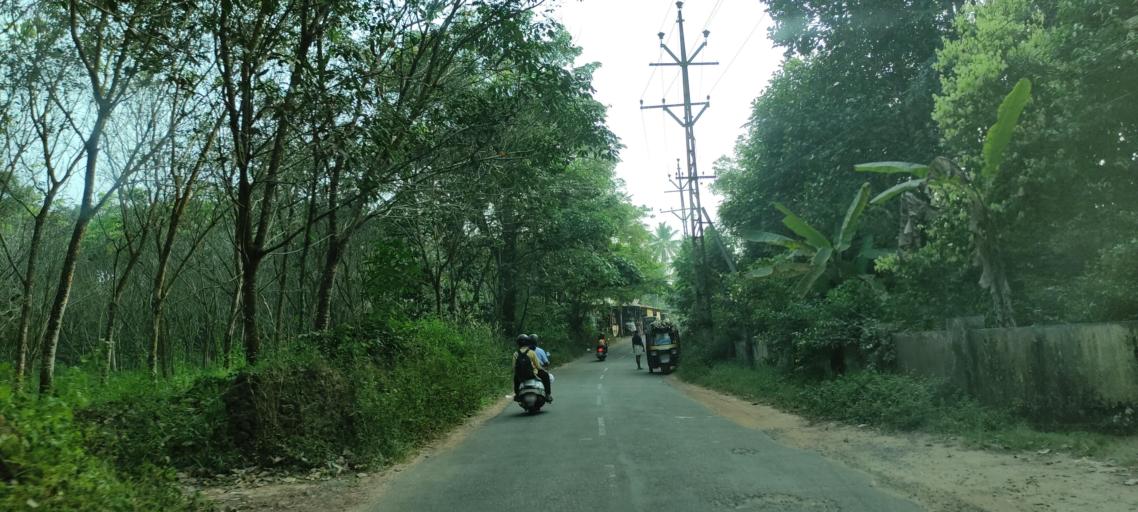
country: IN
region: Kerala
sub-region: Kottayam
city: Vaikam
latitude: 9.7314
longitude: 76.4787
